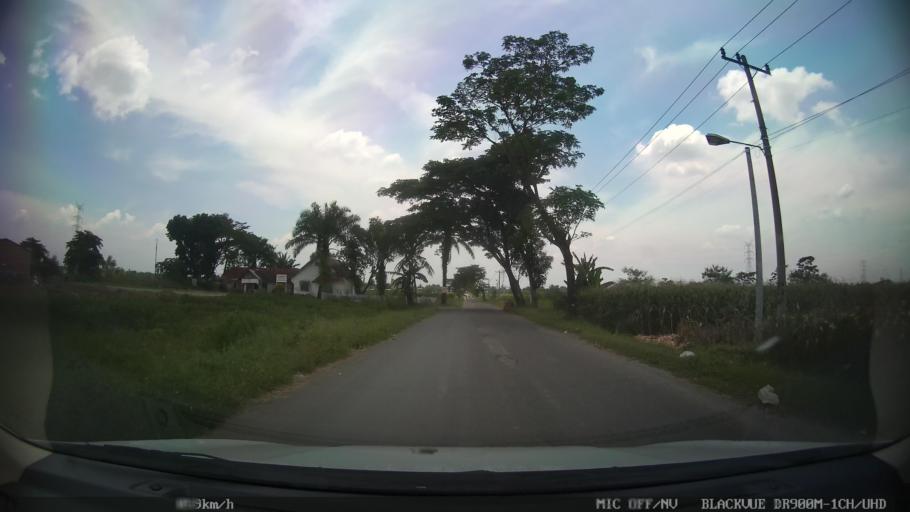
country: ID
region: North Sumatra
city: Binjai
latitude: 3.5921
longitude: 98.5112
